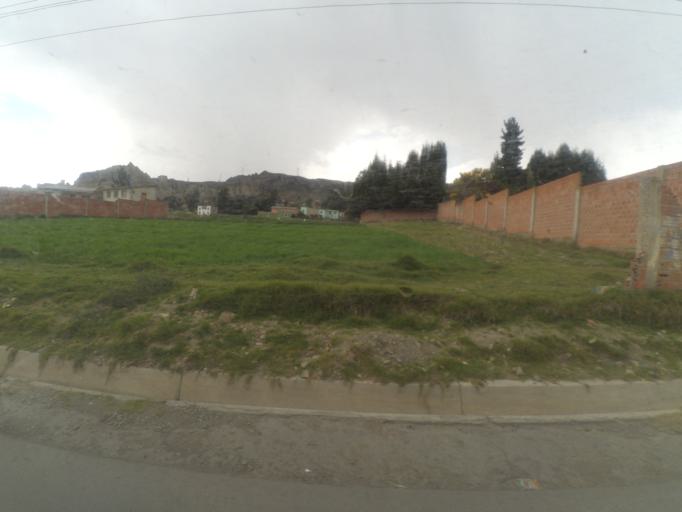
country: BO
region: La Paz
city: La Paz
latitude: -16.5718
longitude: -68.1736
